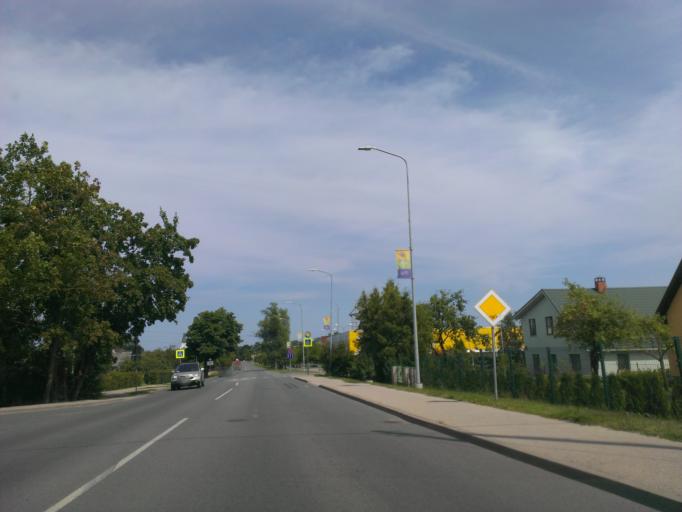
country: LV
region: Salaspils
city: Salaspils
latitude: 56.8544
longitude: 24.3412
